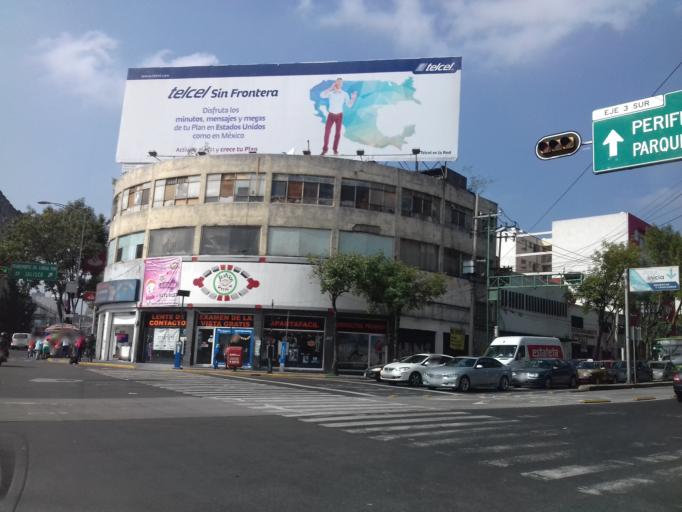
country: MX
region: Mexico City
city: Polanco
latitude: 19.4080
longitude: -99.1844
